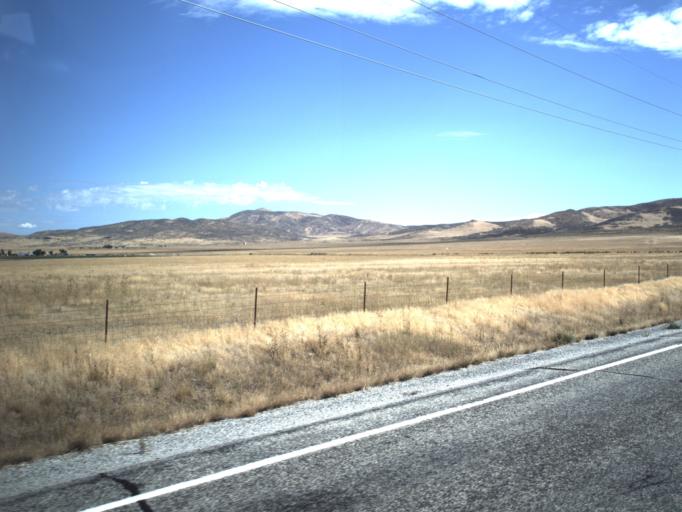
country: US
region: Utah
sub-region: Box Elder County
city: Tremonton
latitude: 41.7224
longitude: -112.4394
